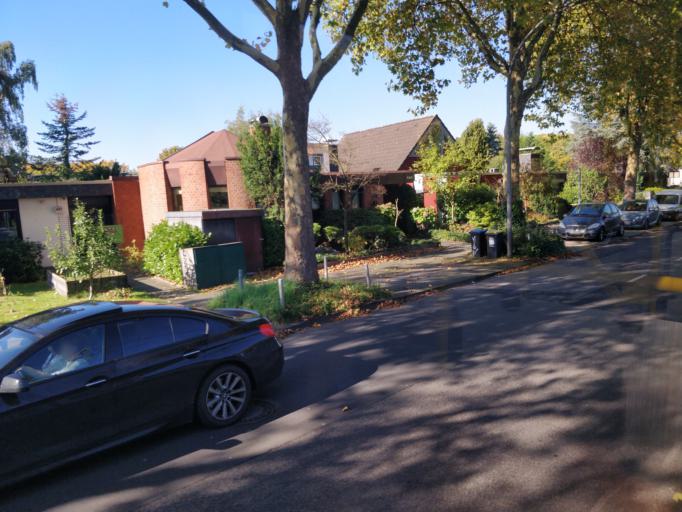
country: DE
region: North Rhine-Westphalia
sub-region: Regierungsbezirk Koln
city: Bilderstoeckchen
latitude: 50.9754
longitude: 6.9042
